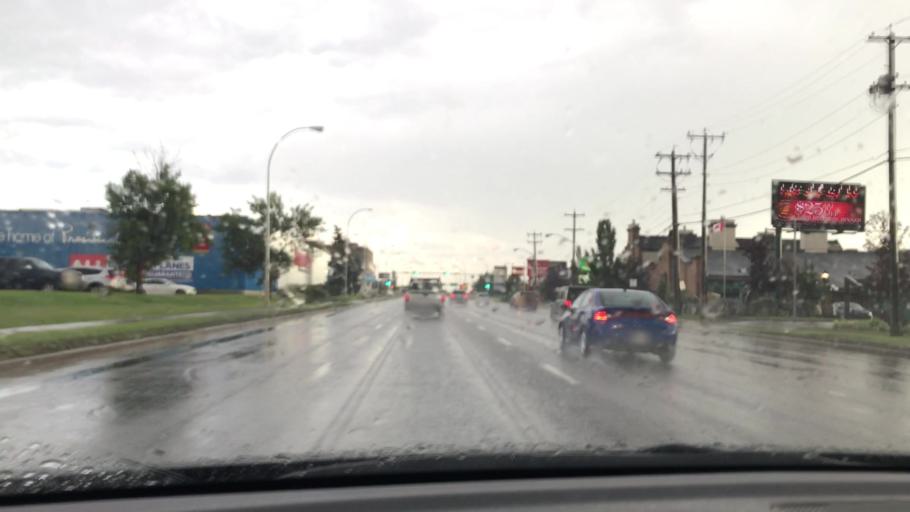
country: CA
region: Alberta
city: Edmonton
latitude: 53.4872
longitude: -113.4949
